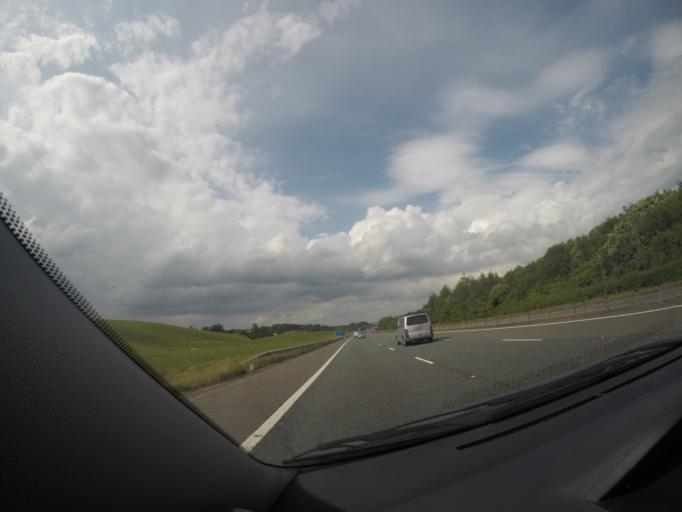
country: GB
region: Scotland
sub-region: Dumfries and Galloway
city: Lochmaben
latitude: 55.2032
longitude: -3.4122
